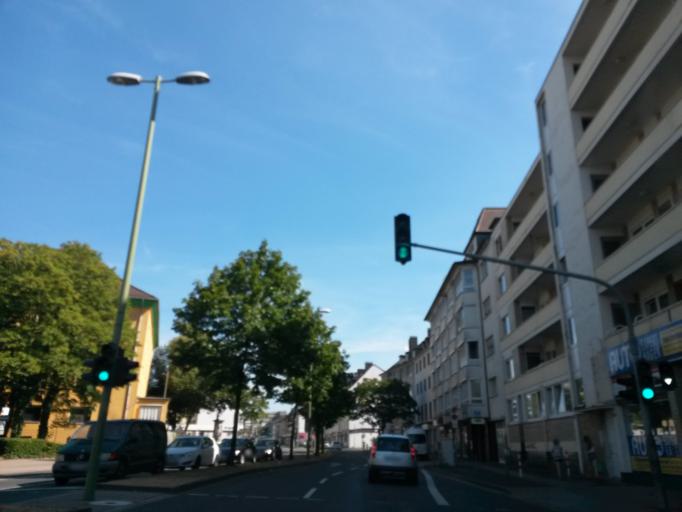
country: DE
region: North Rhine-Westphalia
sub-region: Regierungsbezirk Arnsberg
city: Hagen
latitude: 51.3633
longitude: 7.4643
